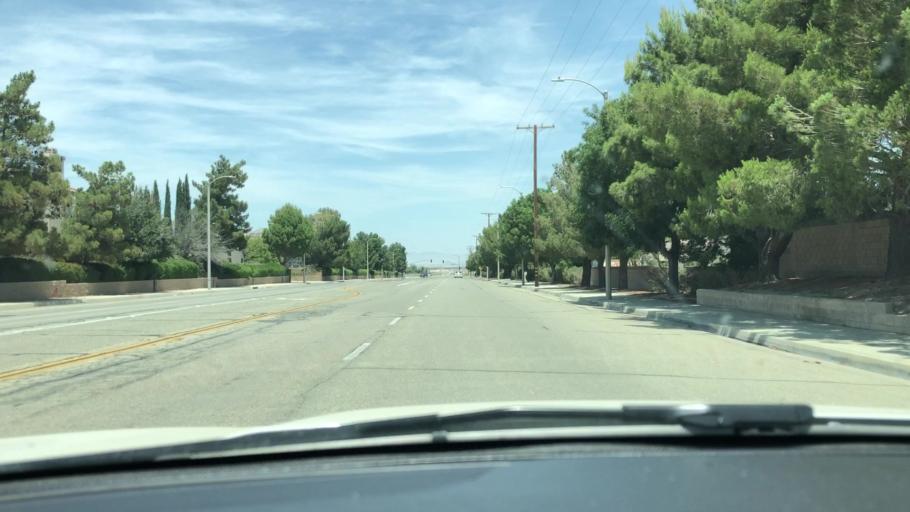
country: US
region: California
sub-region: Los Angeles County
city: Quartz Hill
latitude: 34.6860
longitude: -118.2014
